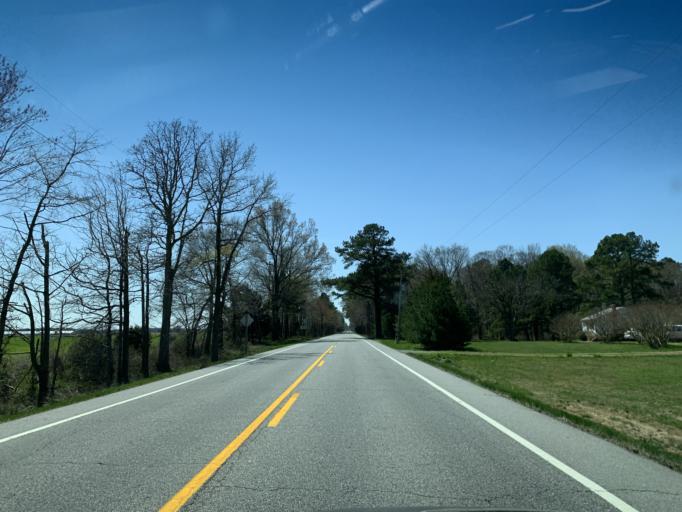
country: US
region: Maryland
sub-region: Talbot County
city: Easton
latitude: 38.8523
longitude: -76.0154
